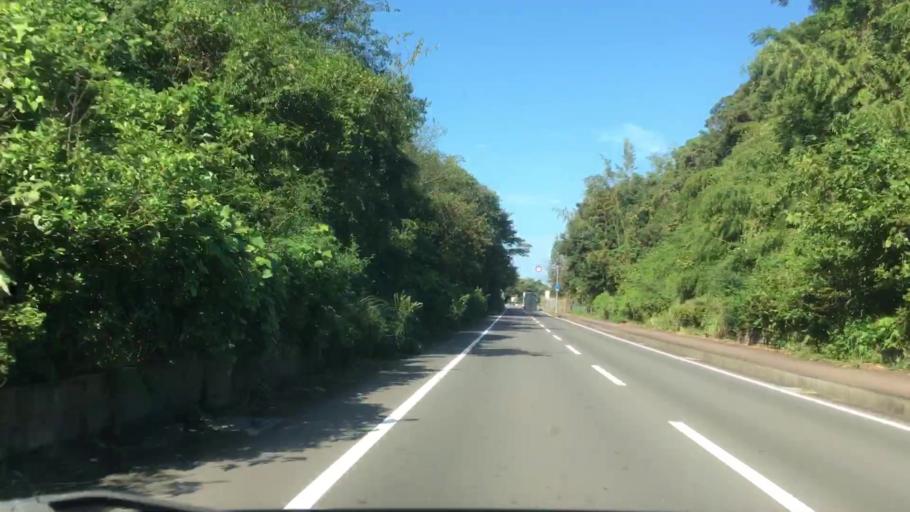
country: JP
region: Nagasaki
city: Sasebo
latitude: 33.0399
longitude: 129.6550
